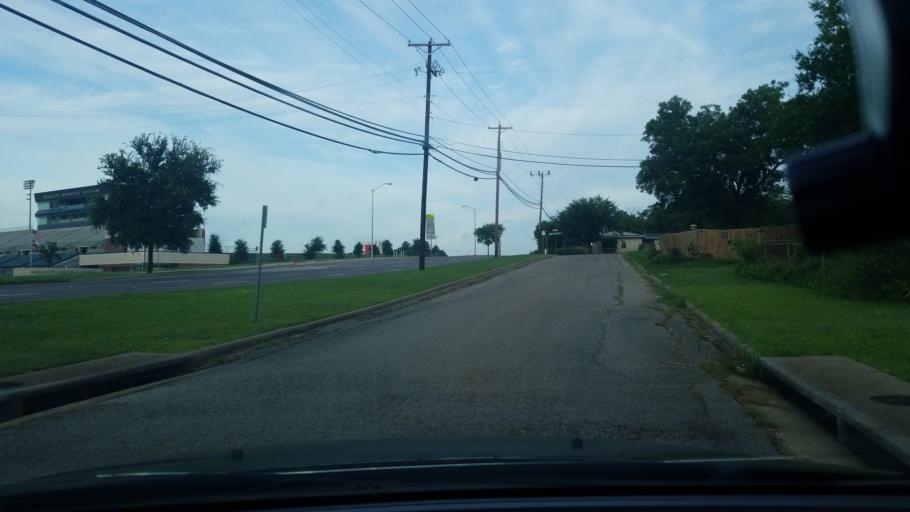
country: US
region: Texas
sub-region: Dallas County
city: Mesquite
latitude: 32.7658
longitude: -96.6341
